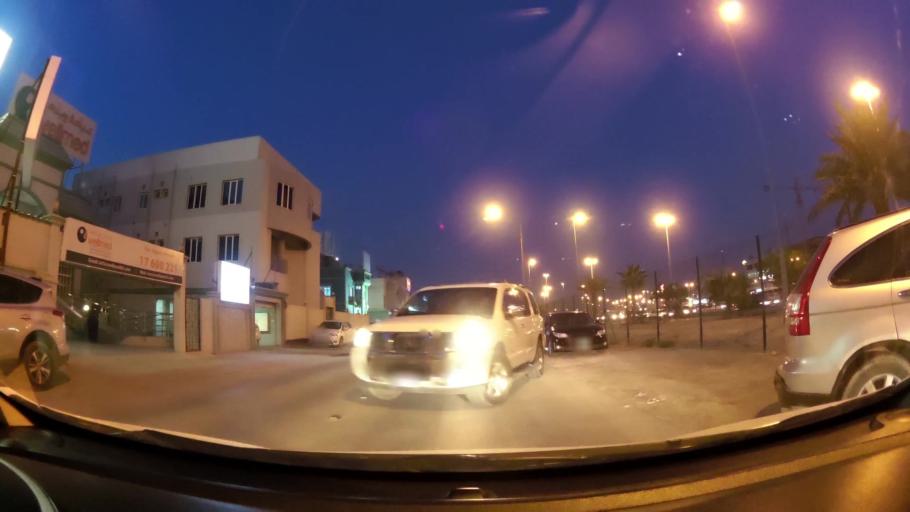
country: BH
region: Manama
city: Jidd Hafs
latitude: 26.2023
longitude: 50.5606
